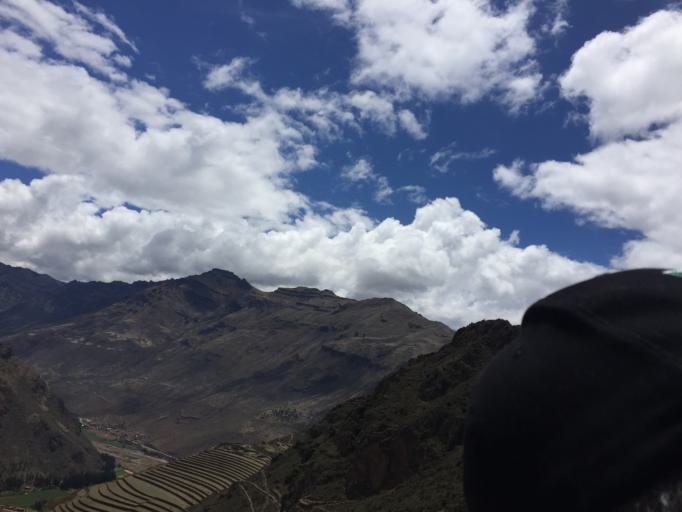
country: PE
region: Cusco
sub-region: Provincia de Calca
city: Pisac
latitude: -13.4070
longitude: -71.8415
